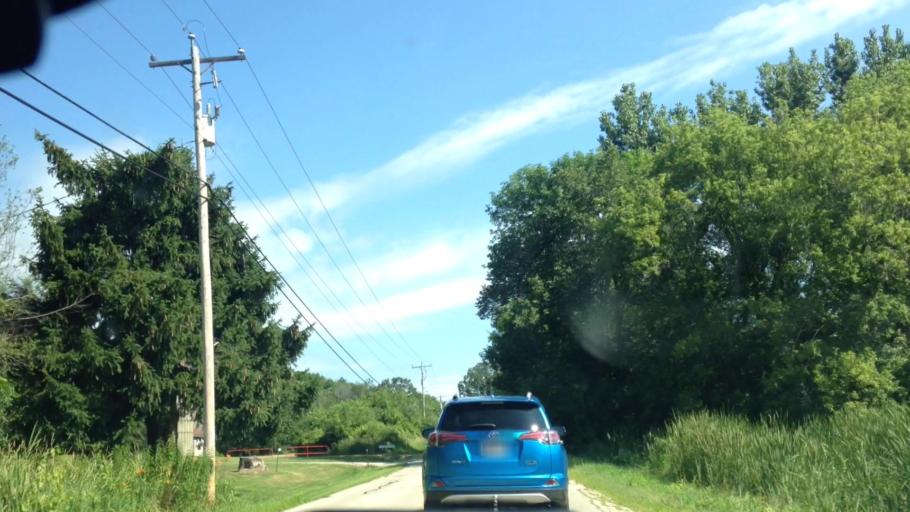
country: US
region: Wisconsin
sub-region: Washington County
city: West Bend
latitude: 43.4142
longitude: -88.2261
